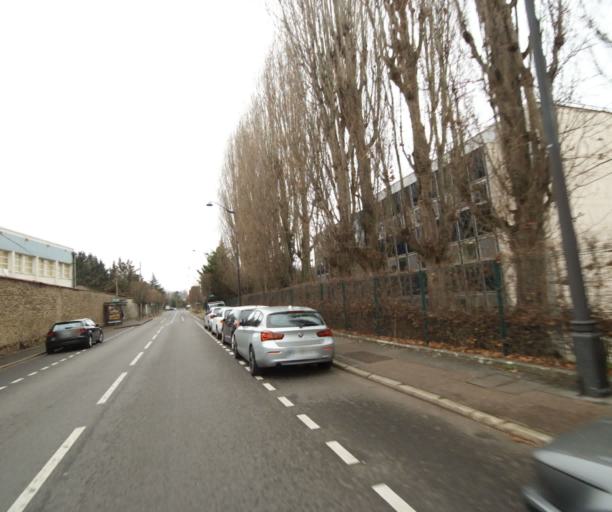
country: FR
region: Ile-de-France
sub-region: Departement des Hauts-de-Seine
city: Garches
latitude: 48.8602
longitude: 2.1786
